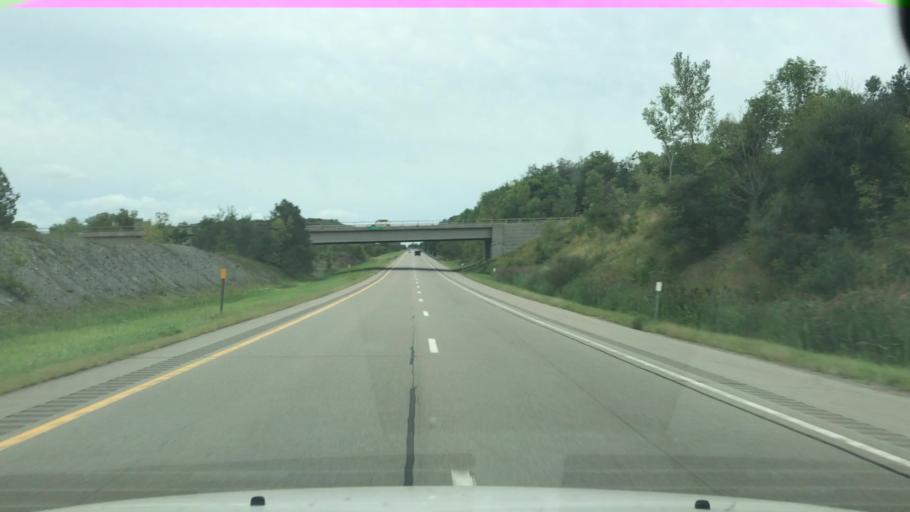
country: US
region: New York
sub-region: Erie County
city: North Boston
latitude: 42.6788
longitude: -78.7850
